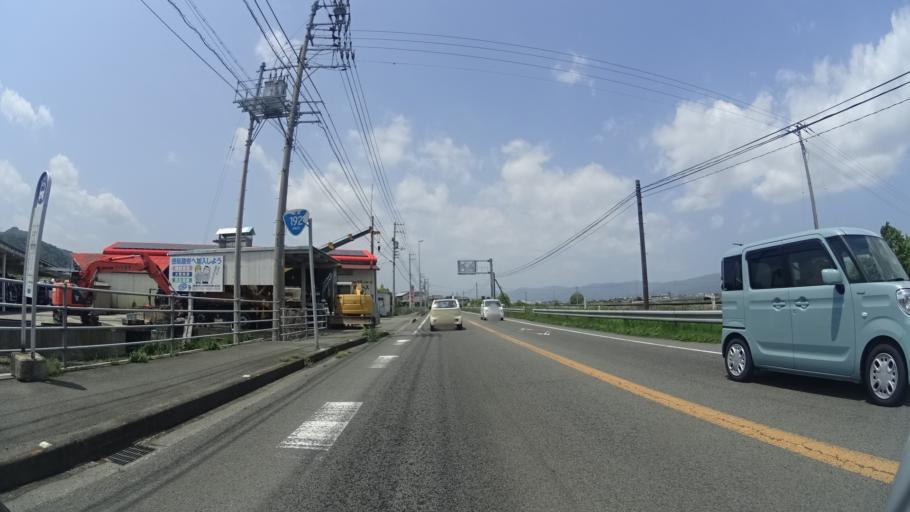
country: JP
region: Tokushima
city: Ishii
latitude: 34.0665
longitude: 134.4273
